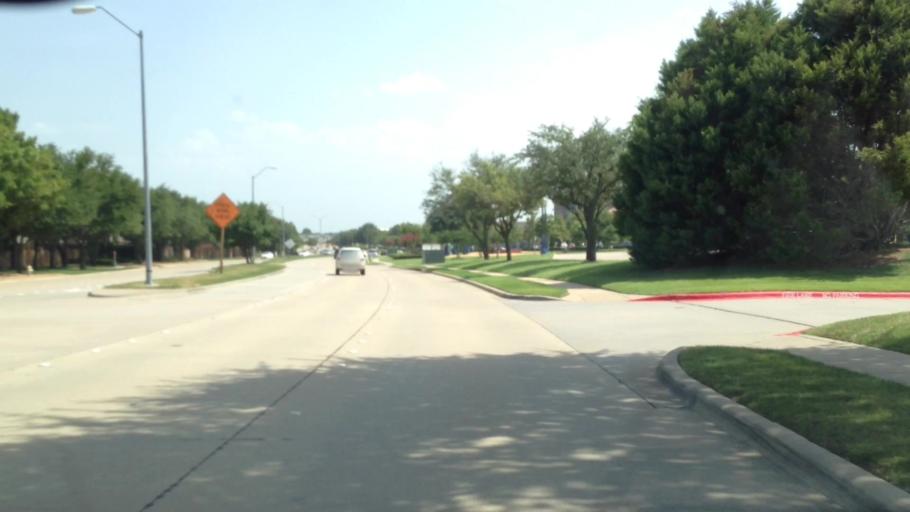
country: US
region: Texas
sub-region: Dallas County
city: Addison
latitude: 33.0372
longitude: -96.8275
